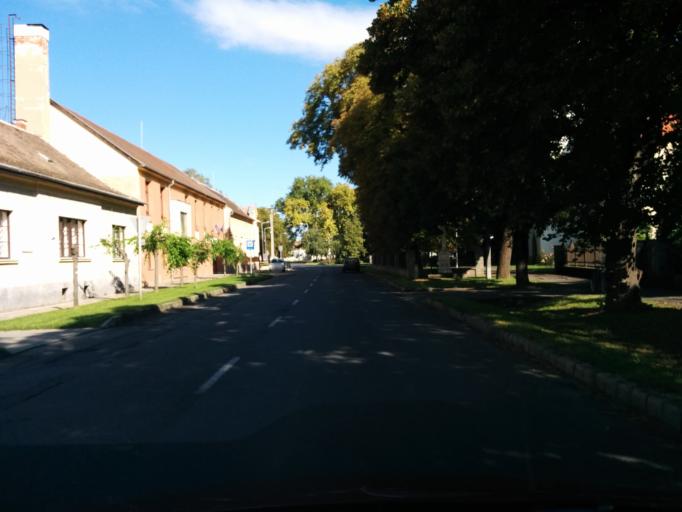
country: HU
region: Vas
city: Csepreg
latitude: 47.4022
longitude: 16.7075
